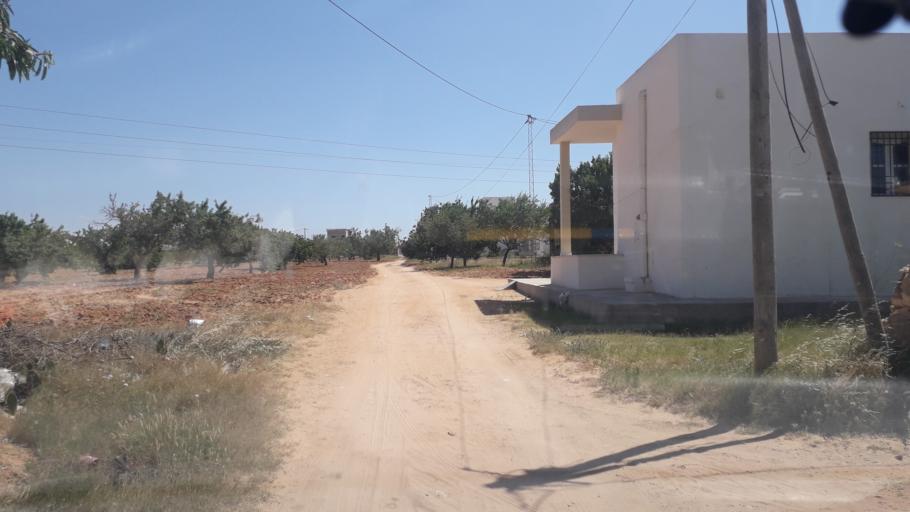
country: TN
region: Safaqis
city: Al Qarmadah
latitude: 34.8327
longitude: 10.7698
